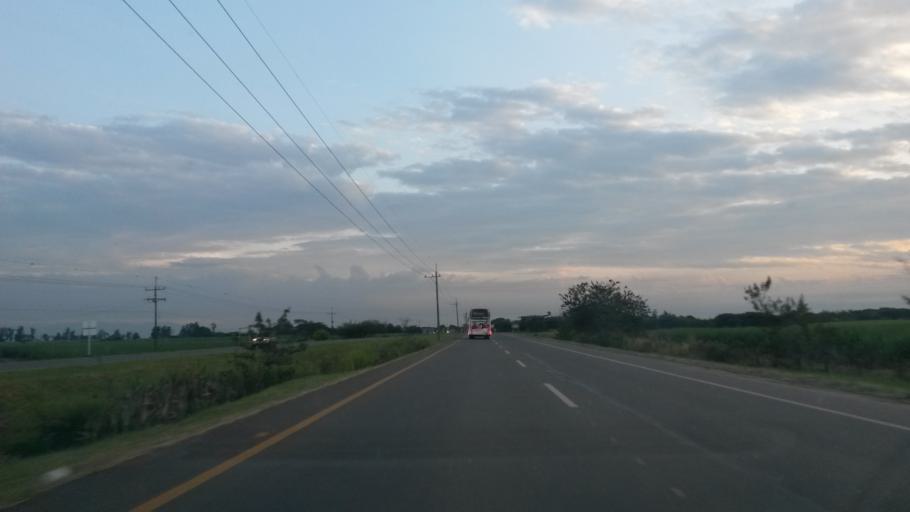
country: CO
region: Cauca
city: Puerto Tejada
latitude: 3.1396
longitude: -76.4621
